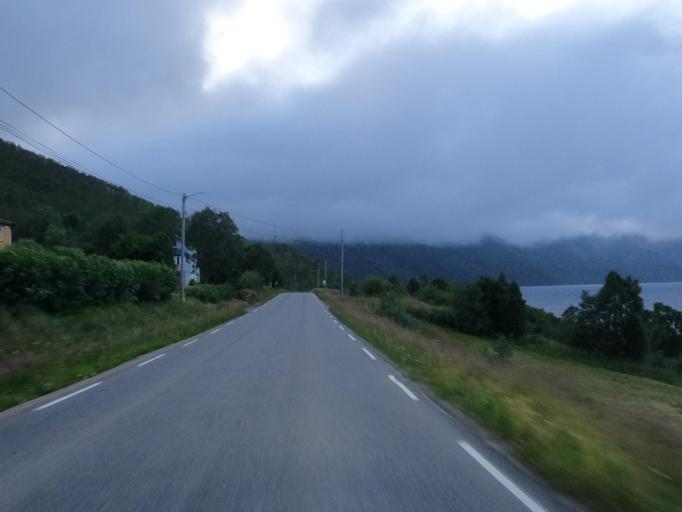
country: NO
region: Nordland
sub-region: Lodingen
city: Lodingen
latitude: 68.6054
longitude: 15.7792
